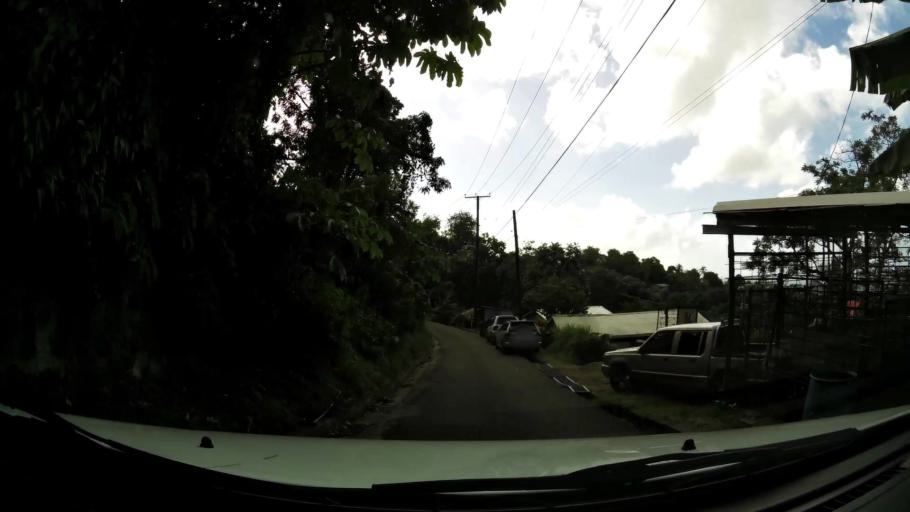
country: LC
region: Castries Quarter
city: Bisee
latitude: 14.0106
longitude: -60.9751
